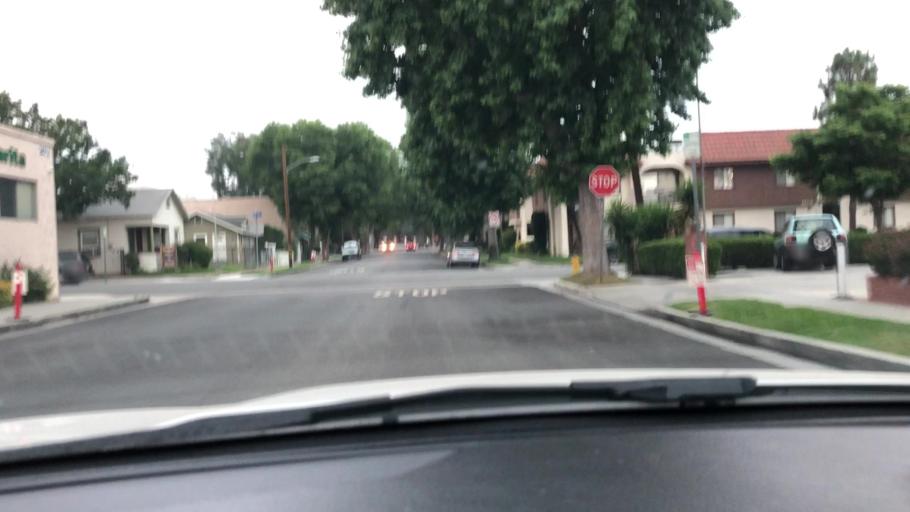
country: US
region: California
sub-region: Los Angeles County
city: Santa Clarita
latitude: 34.3795
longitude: -118.5298
